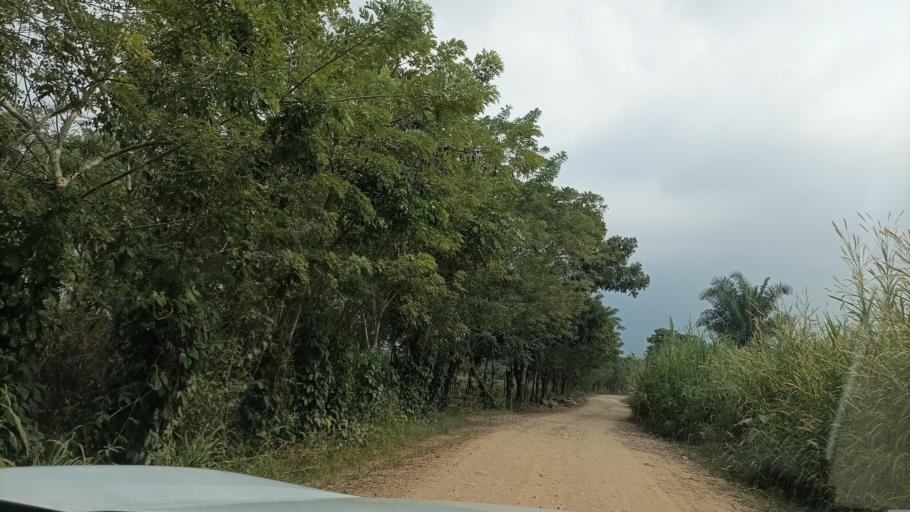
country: MX
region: Veracruz
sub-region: Moloacan
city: Cuichapa
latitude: 17.5834
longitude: -94.2139
